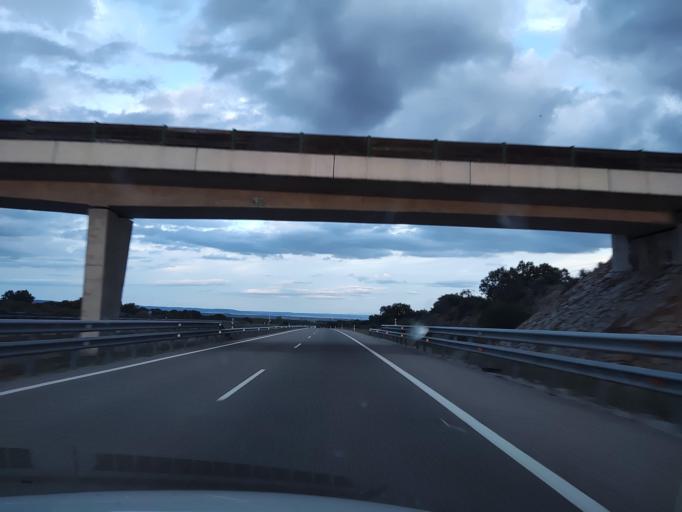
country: ES
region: Castille and Leon
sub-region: Provincia de Salamanca
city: Espeja
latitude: 40.5883
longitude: -6.7454
